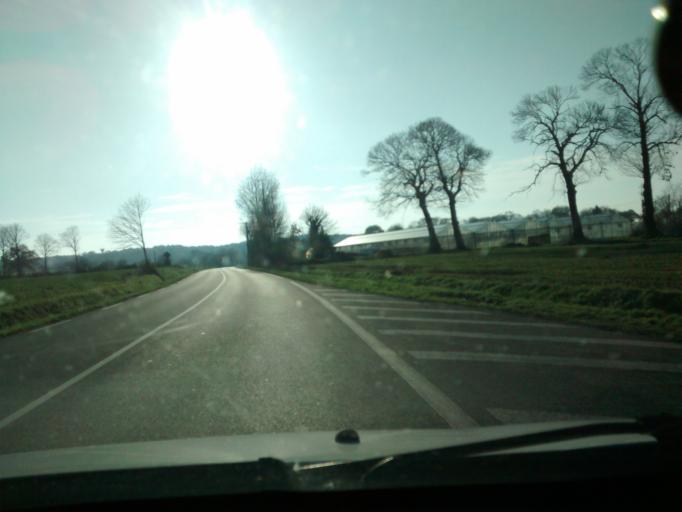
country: FR
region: Brittany
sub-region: Departement d'Ille-et-Vilaine
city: Antrain
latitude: 48.4455
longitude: -1.4764
